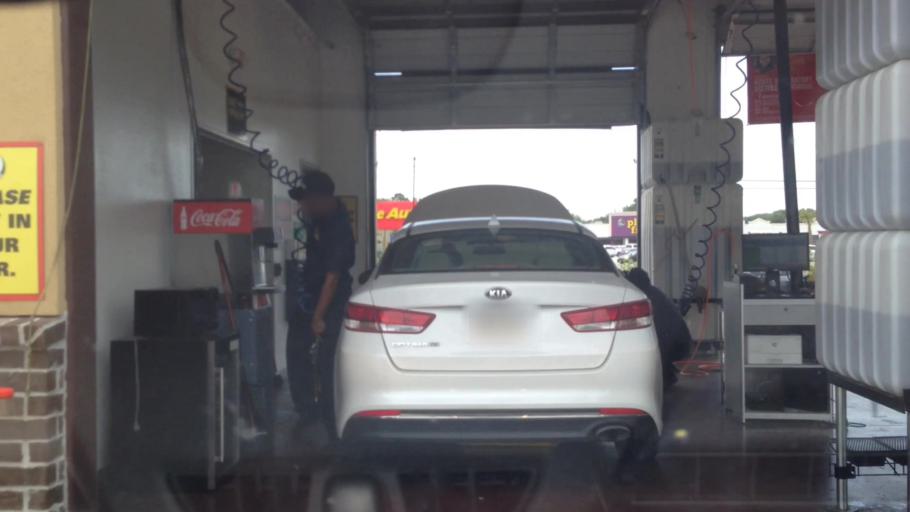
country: US
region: Louisiana
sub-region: Iberia Parish
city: New Iberia
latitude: 29.9884
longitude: -91.8251
